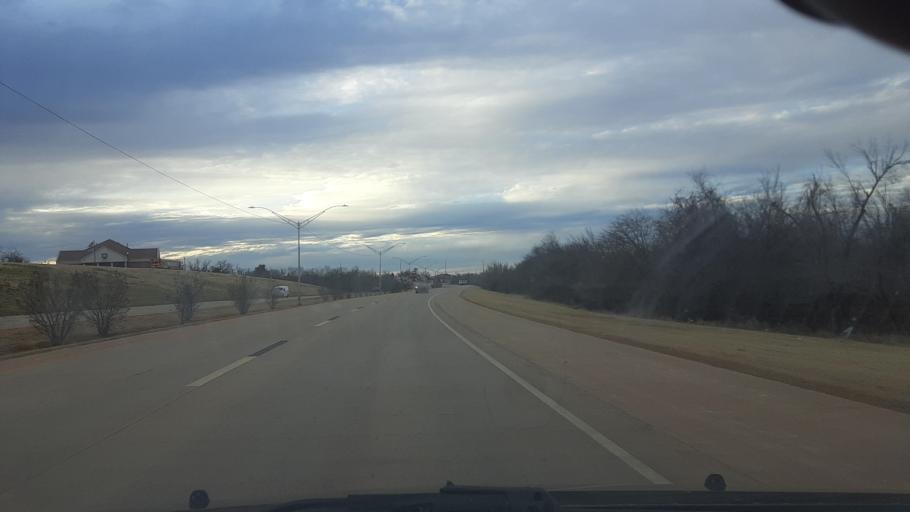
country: US
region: Oklahoma
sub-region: Logan County
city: Guthrie
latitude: 35.8784
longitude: -97.3990
